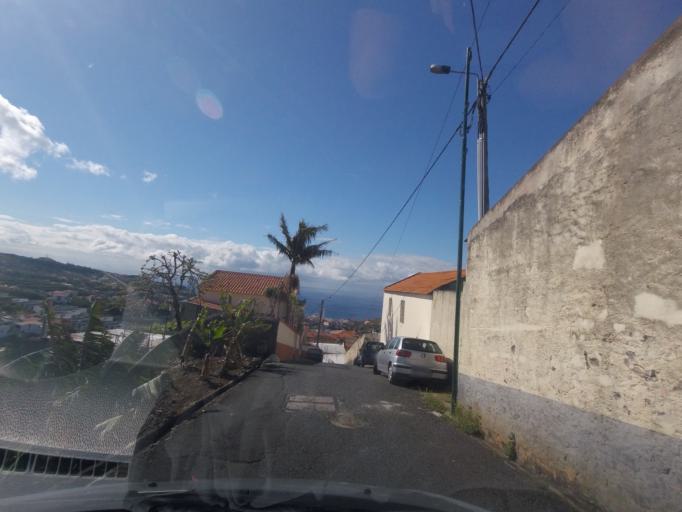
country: PT
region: Madeira
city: Camara de Lobos
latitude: 32.6620
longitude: -16.9739
